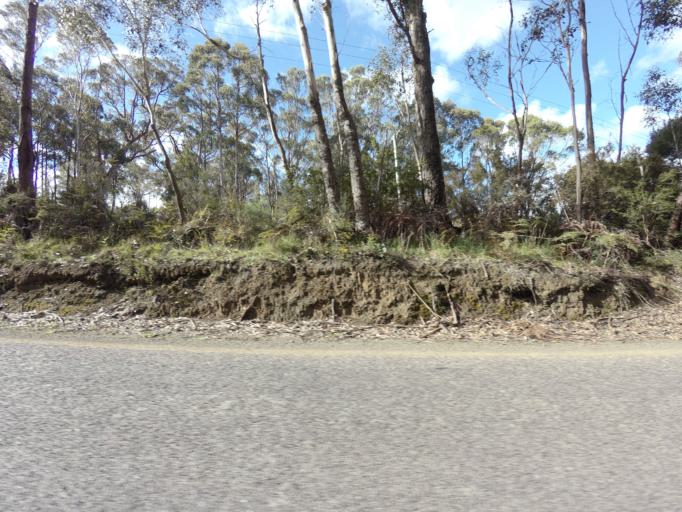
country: AU
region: Tasmania
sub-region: Huon Valley
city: Geeveston
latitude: -43.1989
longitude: 146.9600
